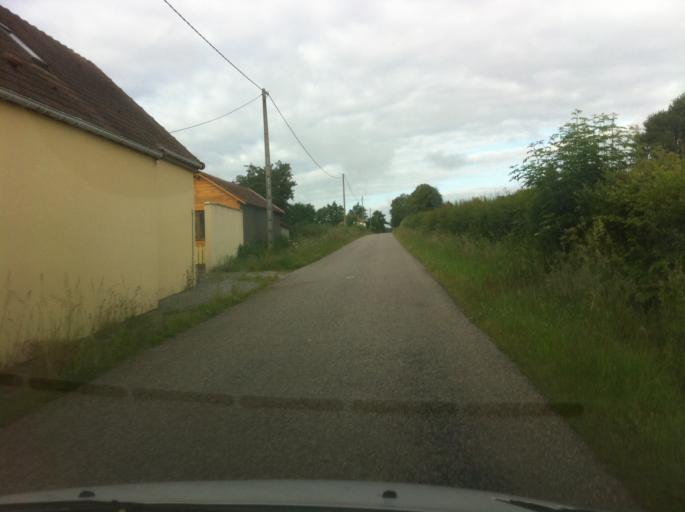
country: FR
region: Auvergne
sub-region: Departement de l'Allier
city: Chantelle
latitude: 46.3280
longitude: 3.1061
